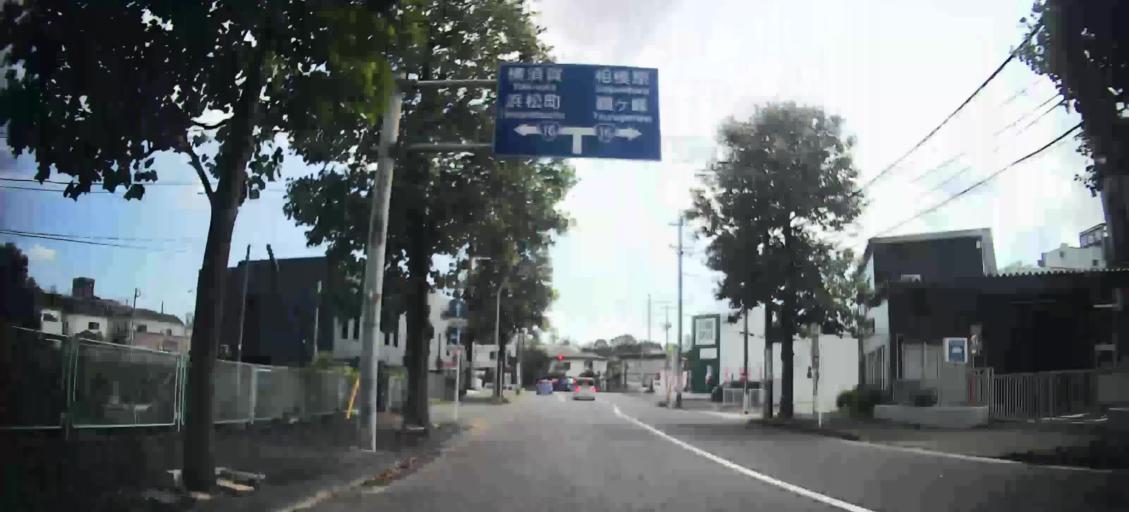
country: JP
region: Kanagawa
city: Yokohama
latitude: 35.4801
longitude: 139.5575
